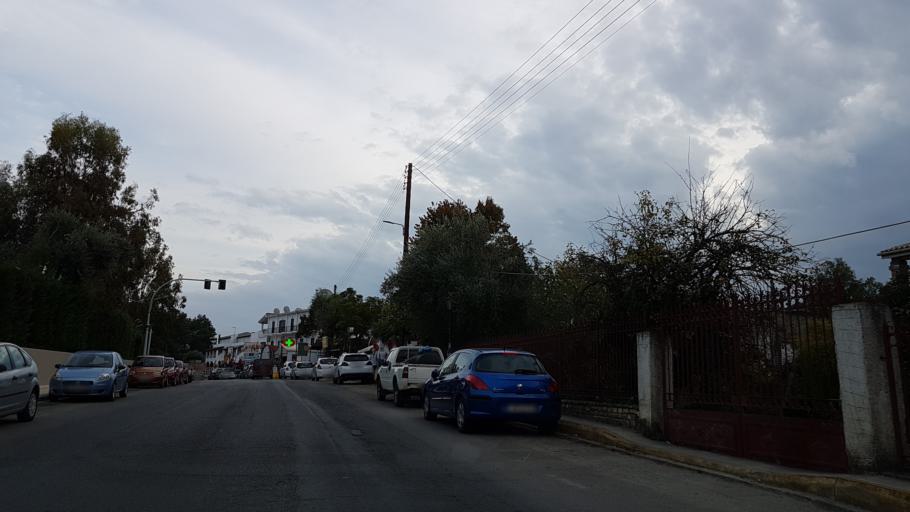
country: GR
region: Ionian Islands
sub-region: Nomos Kerkyras
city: Kontokali
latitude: 39.6785
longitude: 19.8387
